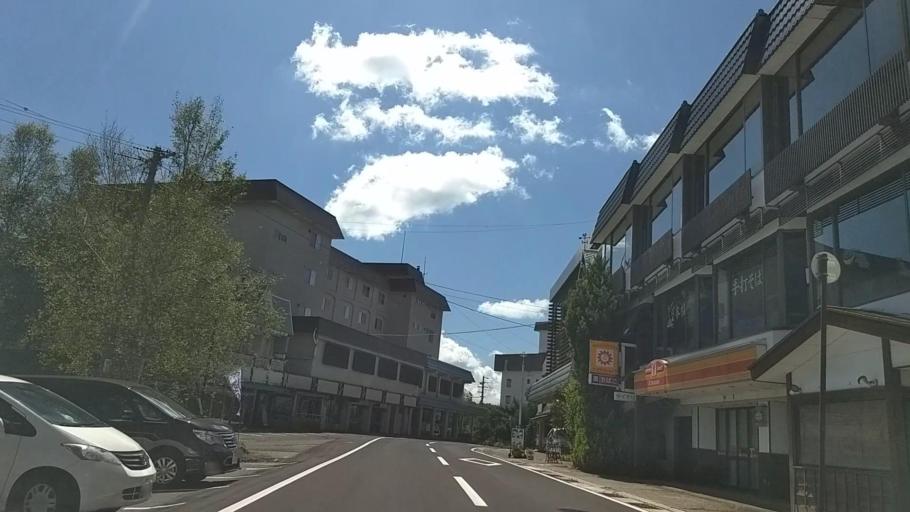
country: JP
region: Nagano
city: Chino
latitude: 36.1063
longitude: 138.2327
